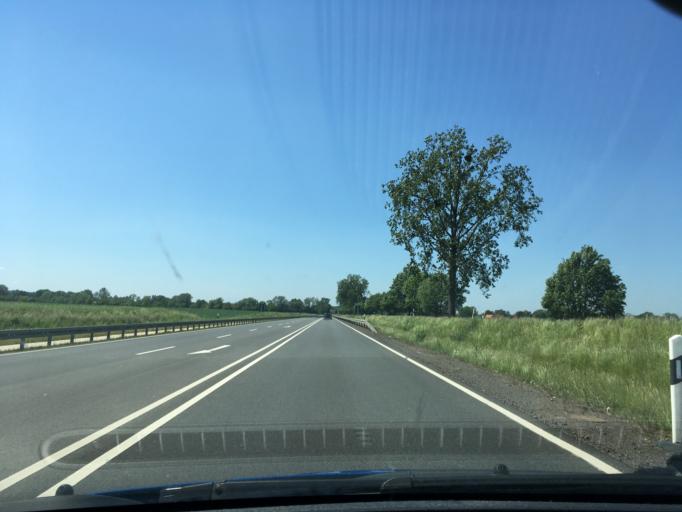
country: DE
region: Lower Saxony
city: Heuerssen
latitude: 52.3342
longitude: 9.2651
